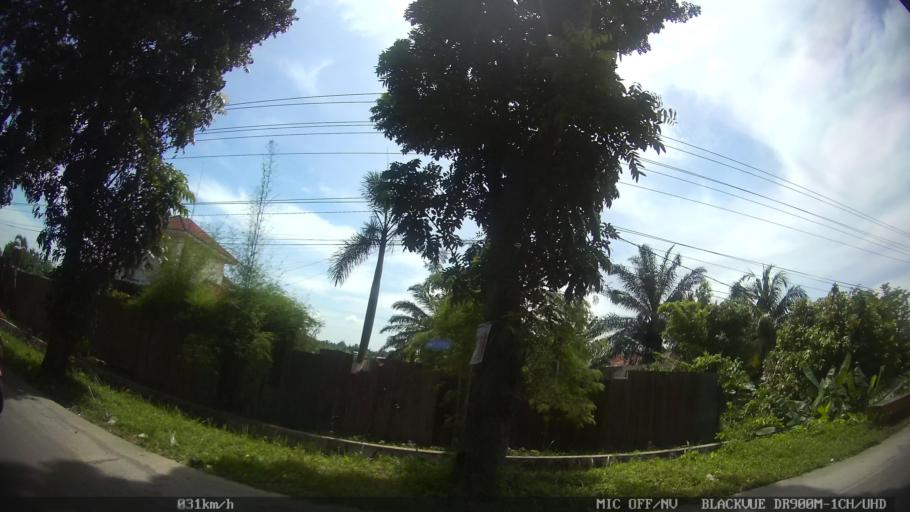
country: ID
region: North Sumatra
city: Binjai
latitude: 3.6390
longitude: 98.5105
